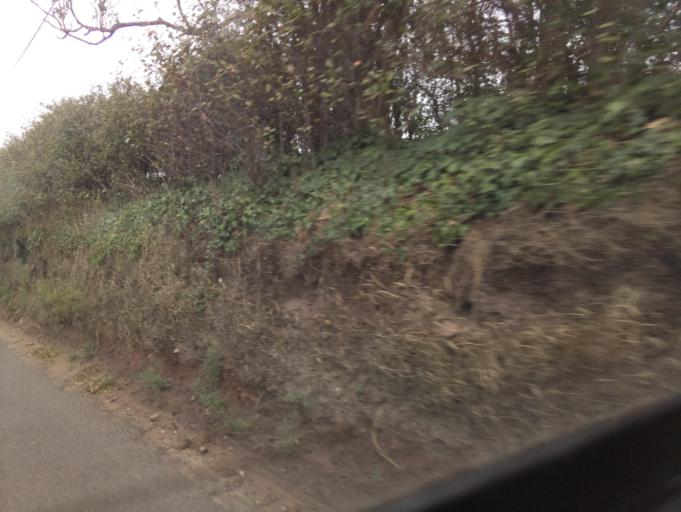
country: GB
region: England
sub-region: Telford and Wrekin
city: Newport
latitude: 52.7984
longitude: -2.3464
